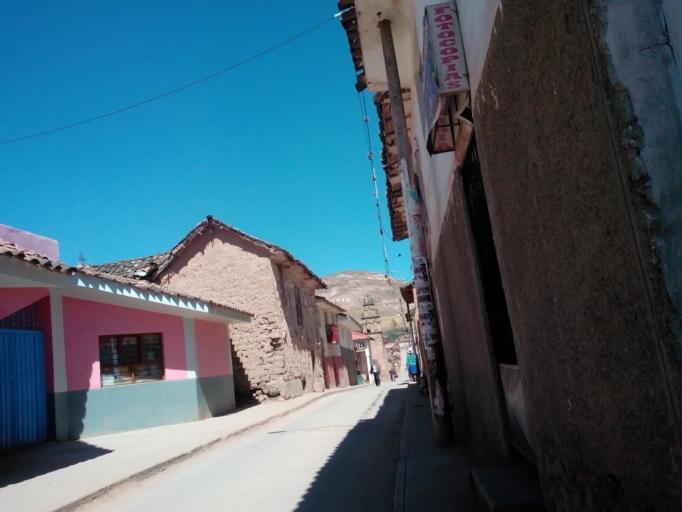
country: PE
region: Cusco
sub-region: Provincia de Urubamba
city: Maras
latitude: -13.3344
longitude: -72.1561
